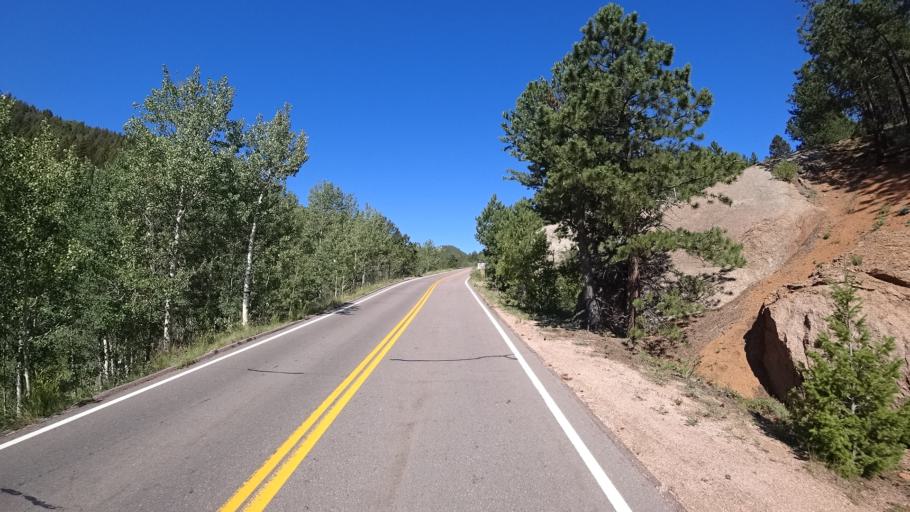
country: US
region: Colorado
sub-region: El Paso County
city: Cascade-Chipita Park
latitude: 38.9034
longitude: -105.0093
